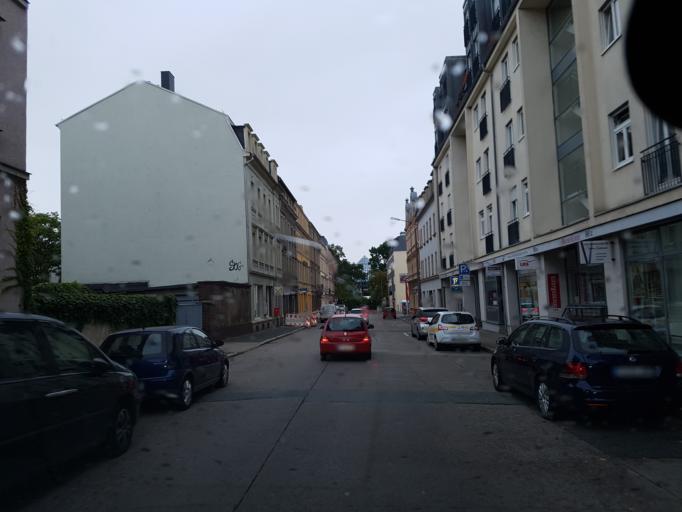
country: DE
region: Saxony
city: Riesa
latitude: 51.3044
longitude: 13.3028
